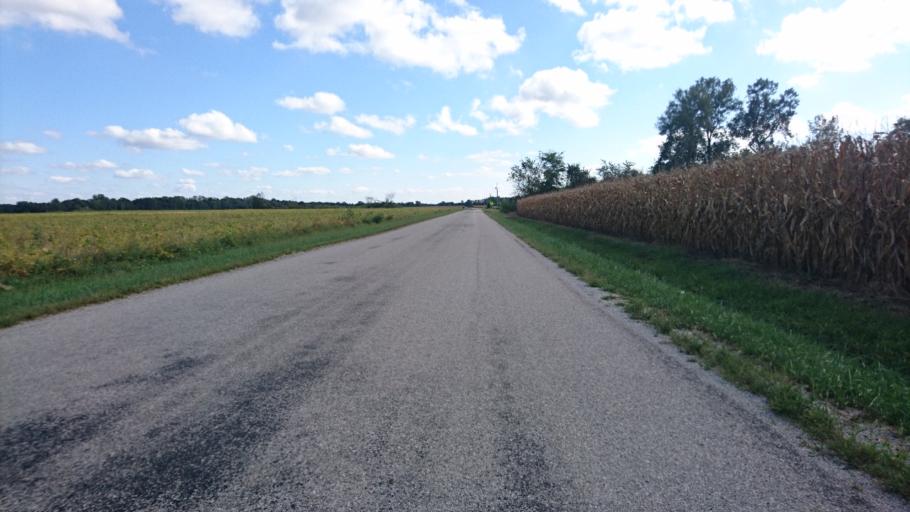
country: US
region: Illinois
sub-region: Macoupin County
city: Staunton
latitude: 39.0072
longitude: -89.7314
